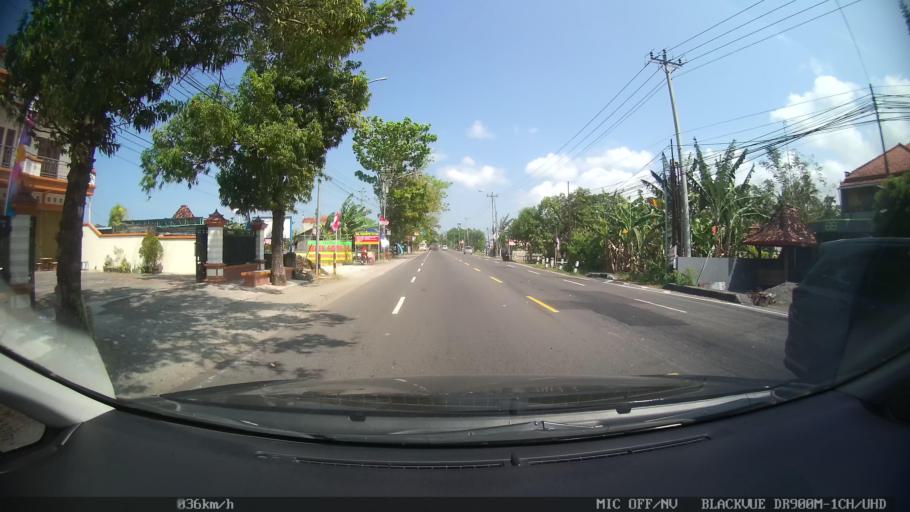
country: ID
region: Daerah Istimewa Yogyakarta
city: Srandakan
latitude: -7.8920
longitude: 110.1279
